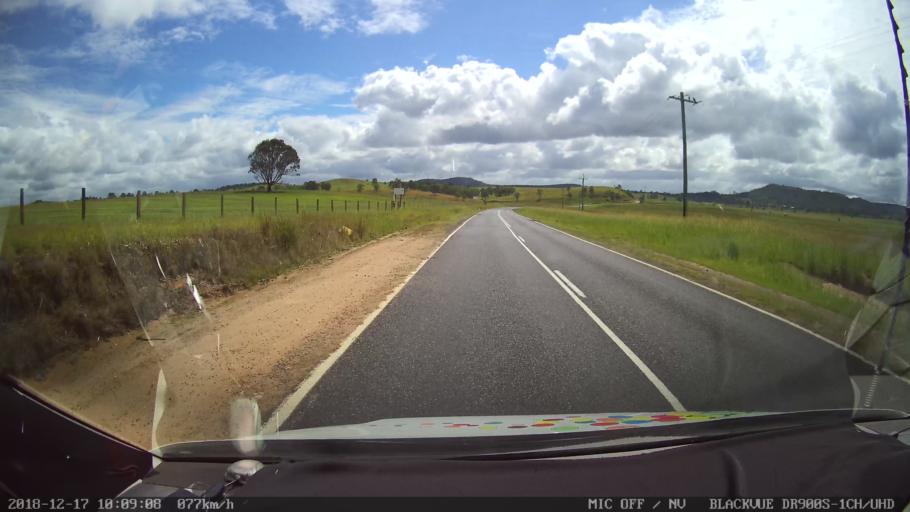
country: AU
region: New South Wales
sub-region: Tenterfield Municipality
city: Carrolls Creek
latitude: -28.8880
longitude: 152.5399
